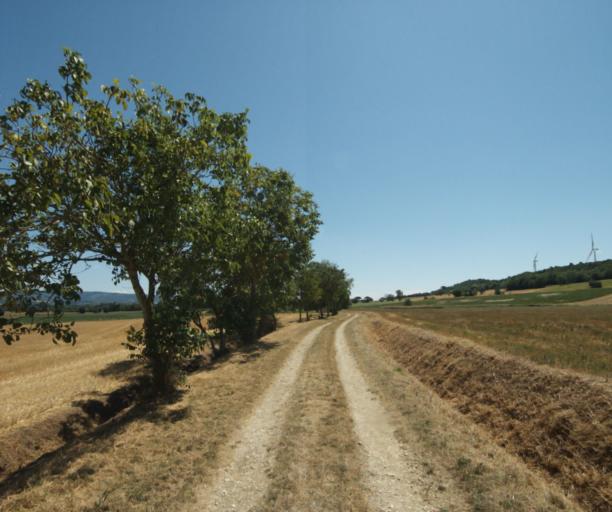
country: FR
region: Midi-Pyrenees
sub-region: Departement de la Haute-Garonne
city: Saint-Felix-Lauragais
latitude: 43.4728
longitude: 1.9232
